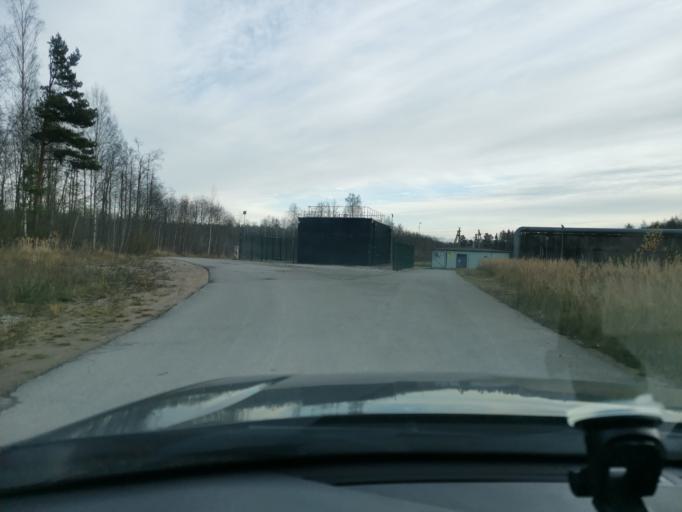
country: EE
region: Ida-Virumaa
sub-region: Sillamaee linn
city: Sillamae
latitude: 59.2608
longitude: 27.9087
